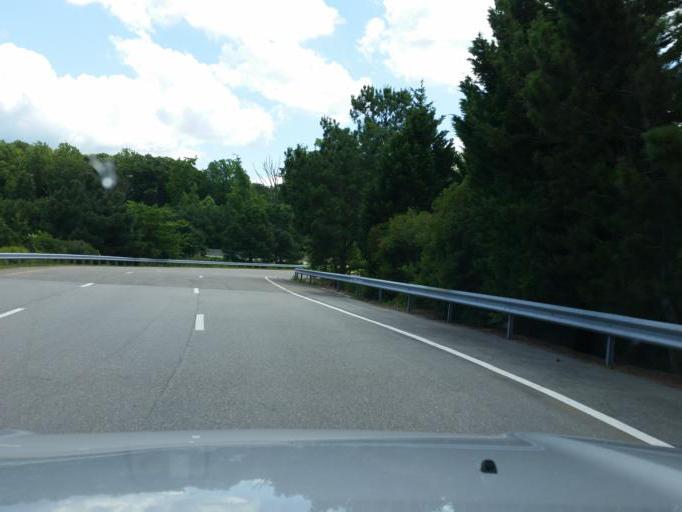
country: US
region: Virginia
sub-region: City of Williamsburg
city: Williamsburg
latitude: 37.2358
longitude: -76.6371
